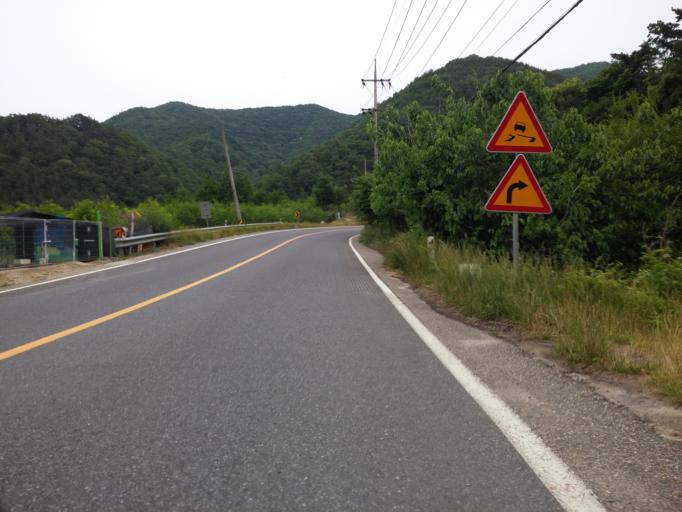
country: KR
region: Chungcheongbuk-do
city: Okcheon
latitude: 36.2437
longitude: 127.5095
